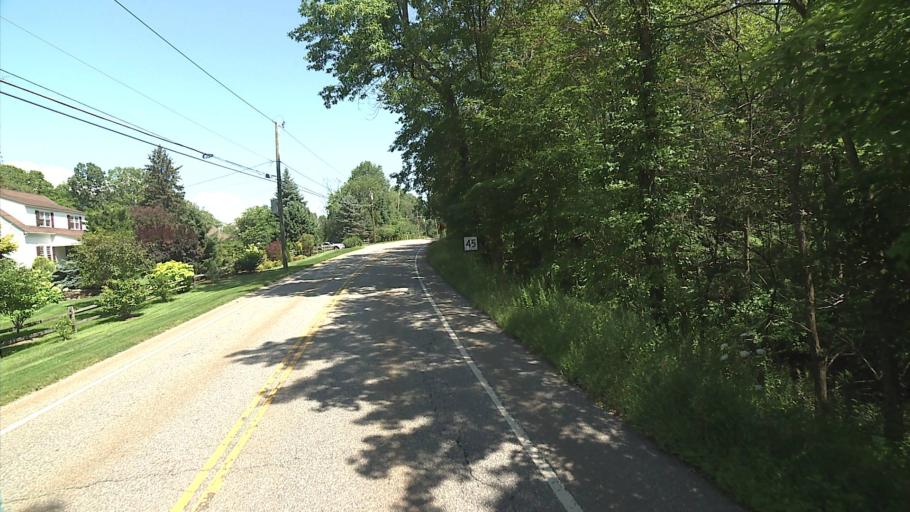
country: US
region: Connecticut
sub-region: Litchfield County
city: New Preston
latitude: 41.7690
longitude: -73.3538
